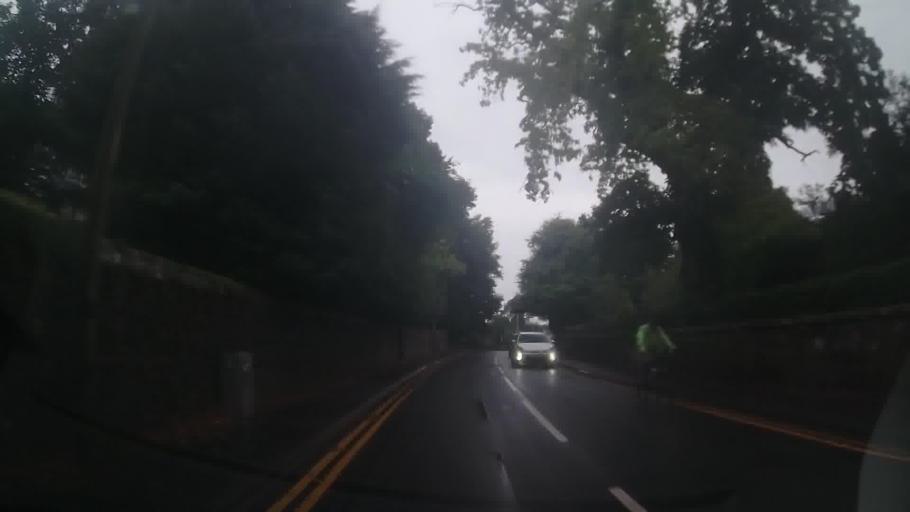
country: GB
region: Scotland
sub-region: North Ayrshire
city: Fairlie
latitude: 55.7555
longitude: -4.8540
